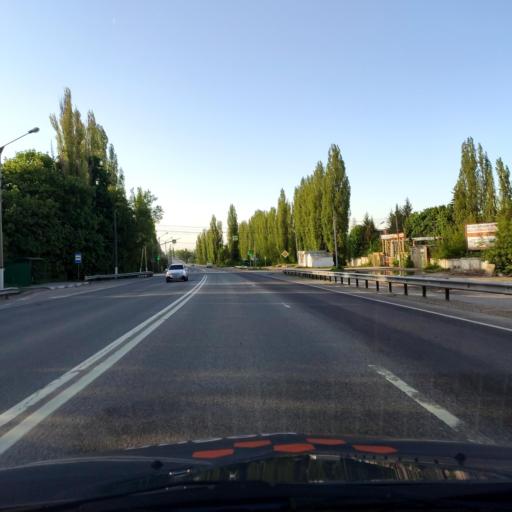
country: RU
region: Lipetsk
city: Yelets
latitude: 52.6094
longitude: 38.4637
